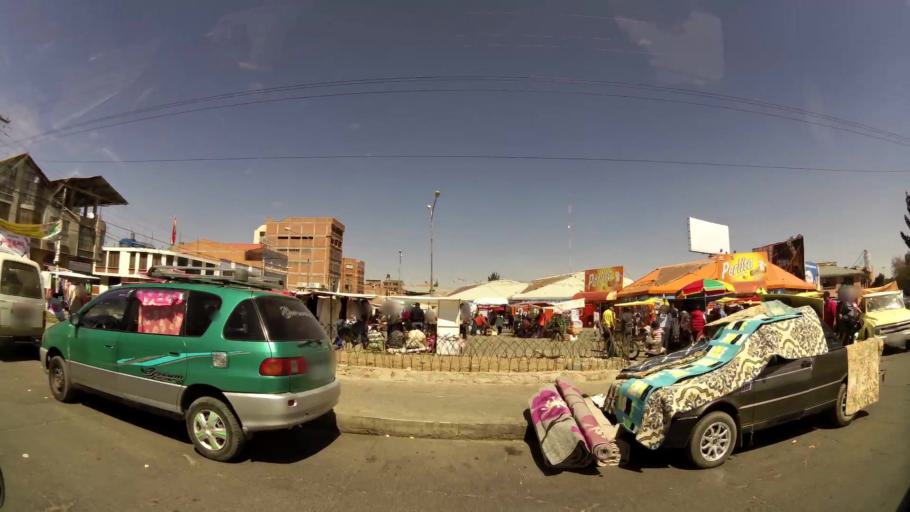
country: BO
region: La Paz
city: La Paz
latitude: -16.5243
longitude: -68.1502
